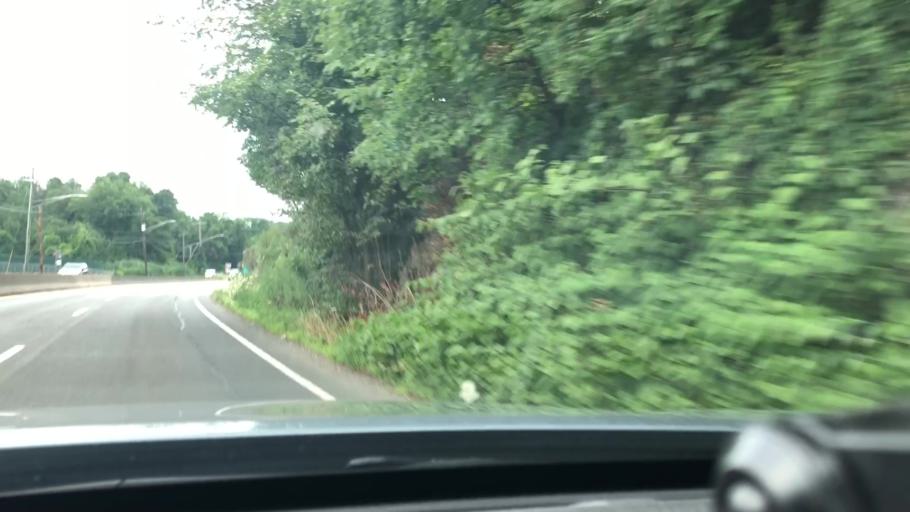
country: US
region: New York
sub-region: Rockland County
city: West Nyack
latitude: 41.0903
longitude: -73.9503
